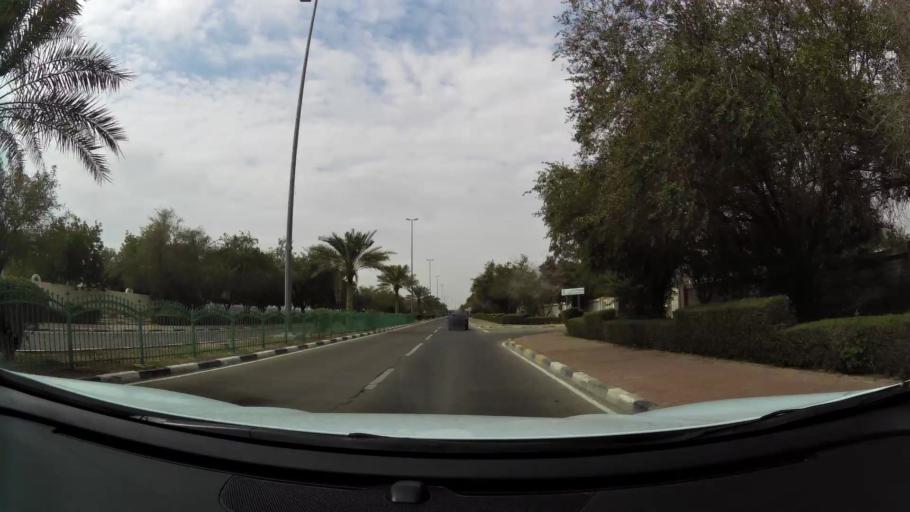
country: OM
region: Al Buraimi
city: Al Buraymi
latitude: 24.2093
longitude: 55.7989
